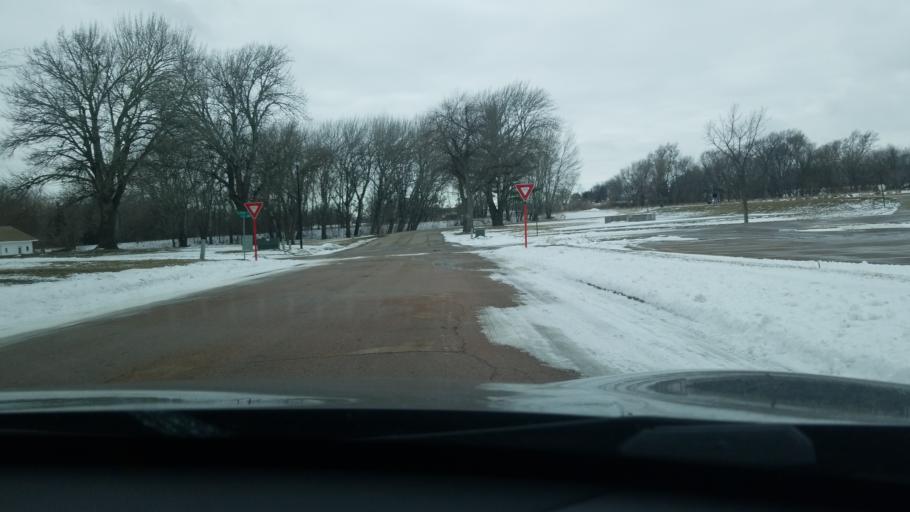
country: US
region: Iowa
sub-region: Lyon County
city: Rock Rapids
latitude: 43.4350
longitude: -96.1688
